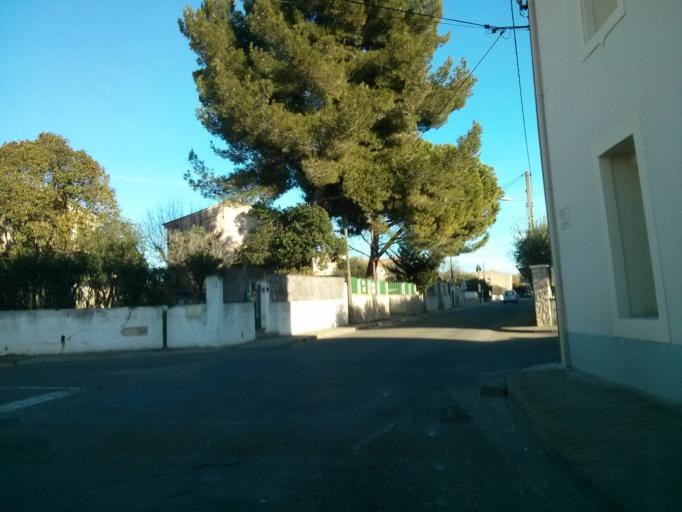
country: FR
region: Languedoc-Roussillon
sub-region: Departement du Gard
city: Vergeze
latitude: 43.7442
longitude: 4.2142
